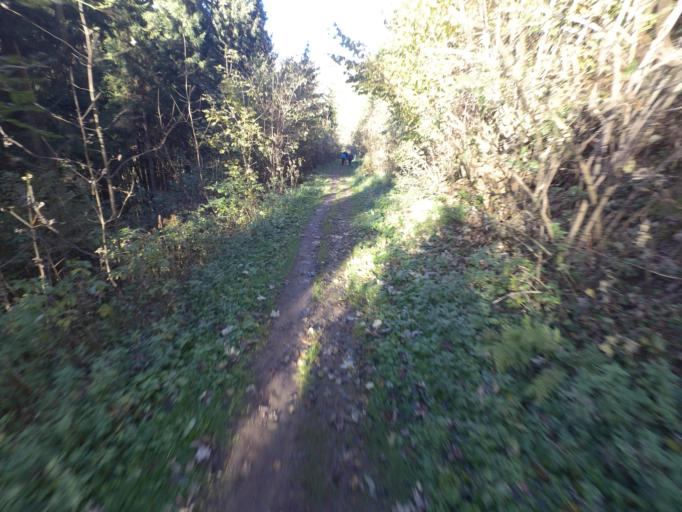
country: AT
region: Salzburg
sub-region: Politischer Bezirk Sankt Johann im Pongau
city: Sankt Johann im Pongau
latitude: 47.3420
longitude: 13.2198
